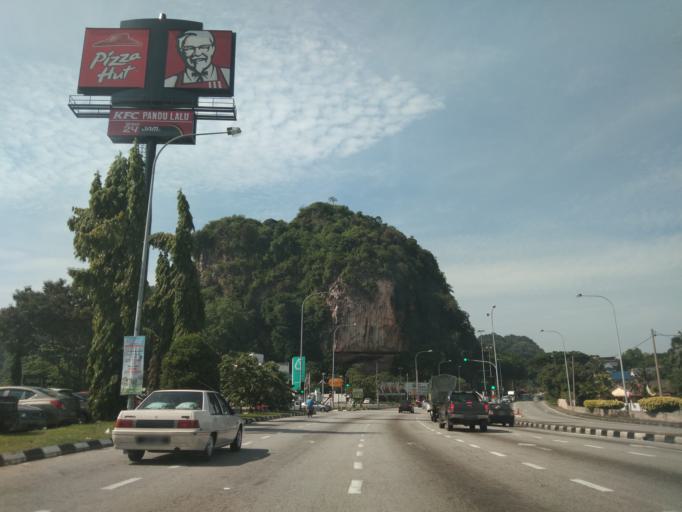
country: MY
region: Perak
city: Ipoh
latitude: 4.5695
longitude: 101.1135
